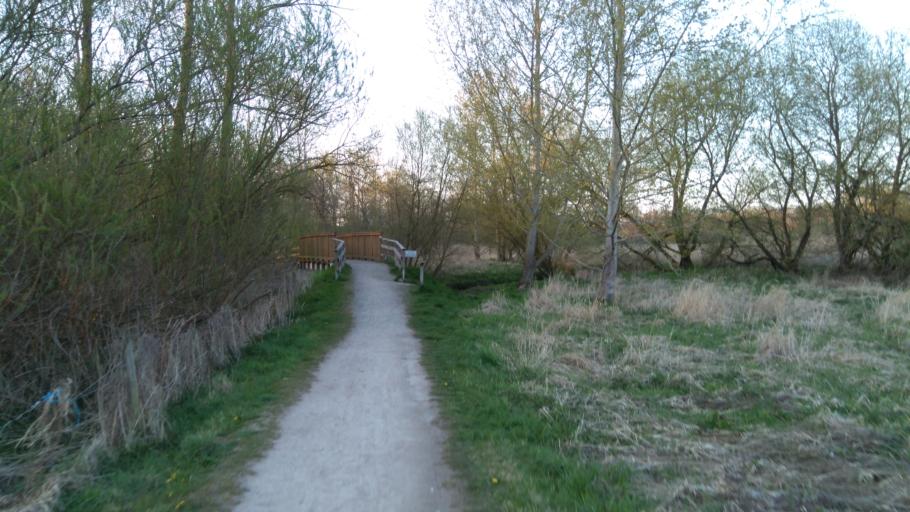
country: DE
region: Lower Saxony
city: Harsefeld
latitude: 53.4753
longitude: 9.5246
